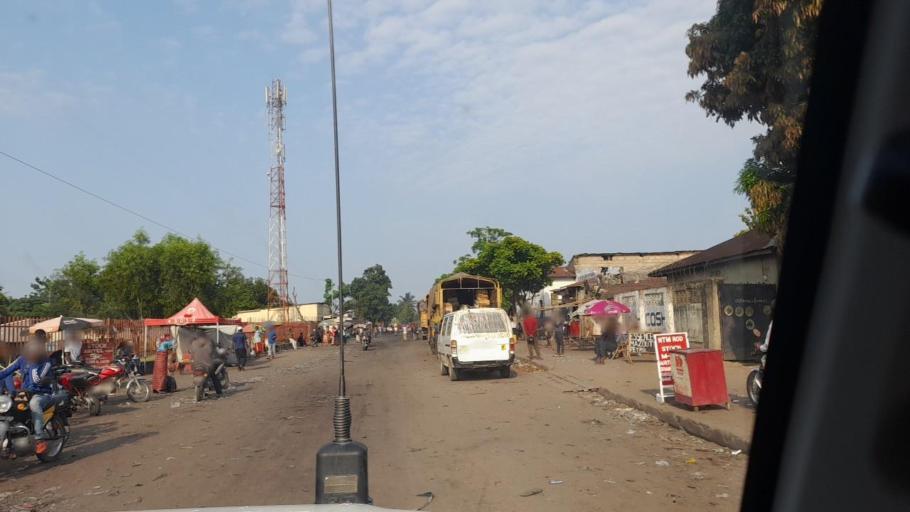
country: CD
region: Kasai-Occidental
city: Kananga
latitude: -5.8950
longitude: 22.3915
